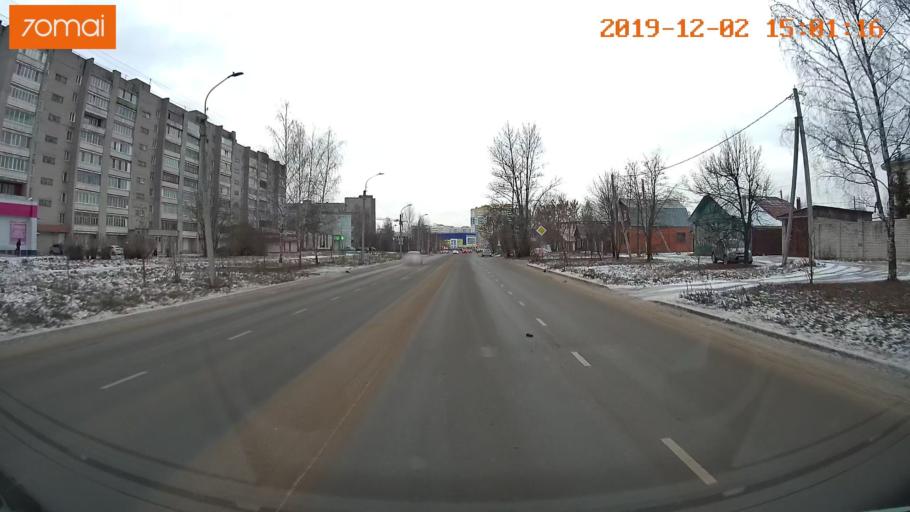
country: RU
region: Ivanovo
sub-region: Gorod Ivanovo
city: Ivanovo
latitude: 56.9736
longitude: 40.9999
